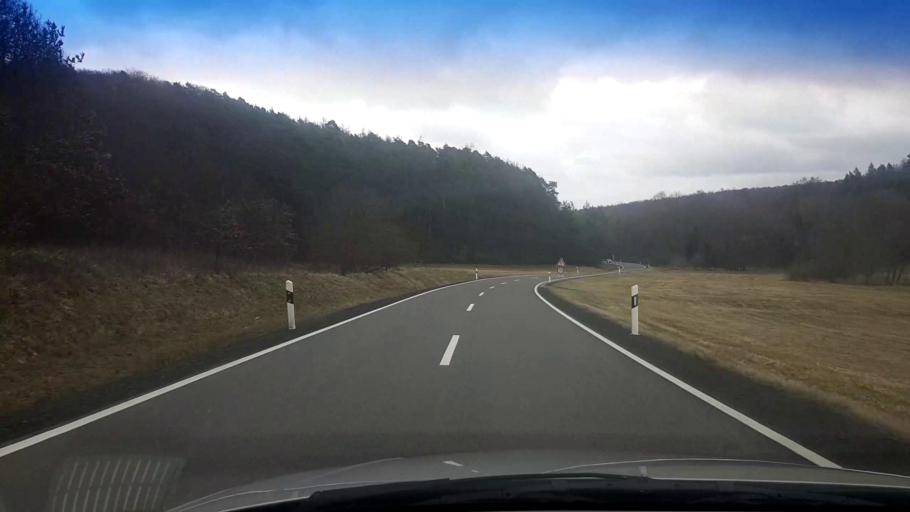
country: DE
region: Bavaria
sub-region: Regierungsbezirk Unterfranken
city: Sand
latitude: 49.9408
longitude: 10.6161
